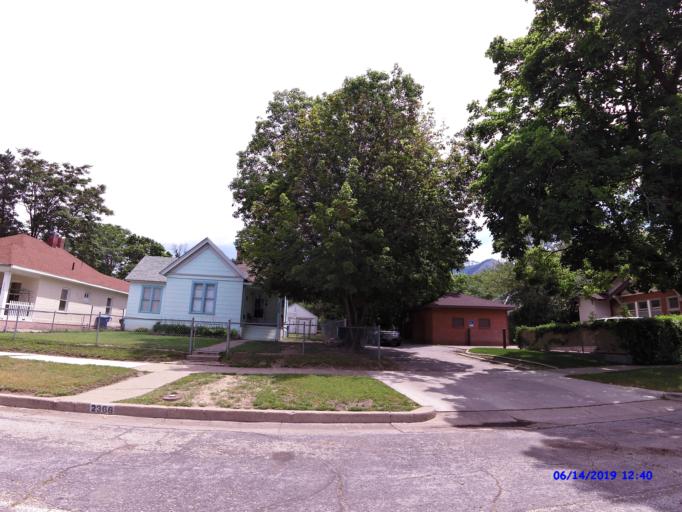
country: US
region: Utah
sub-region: Weber County
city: Ogden
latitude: 41.2230
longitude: -111.9537
